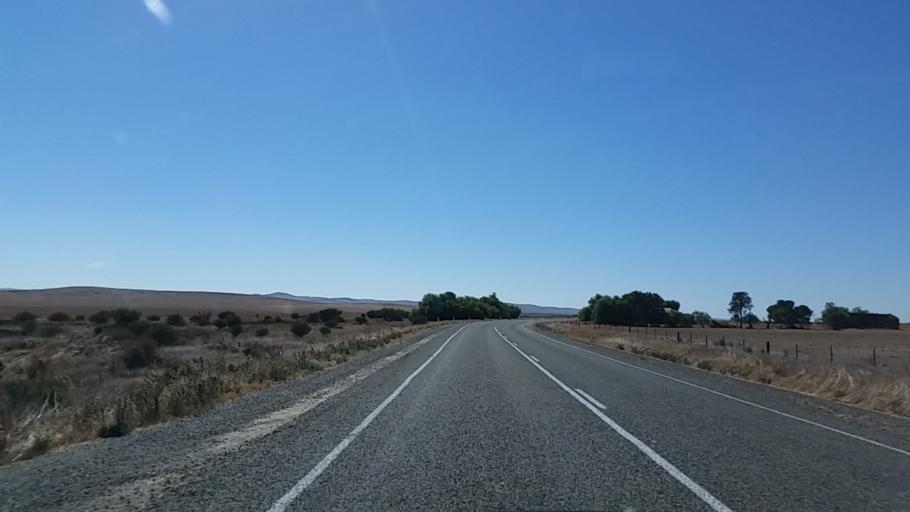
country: AU
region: South Australia
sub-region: Northern Areas
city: Jamestown
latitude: -33.2843
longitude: 138.8694
